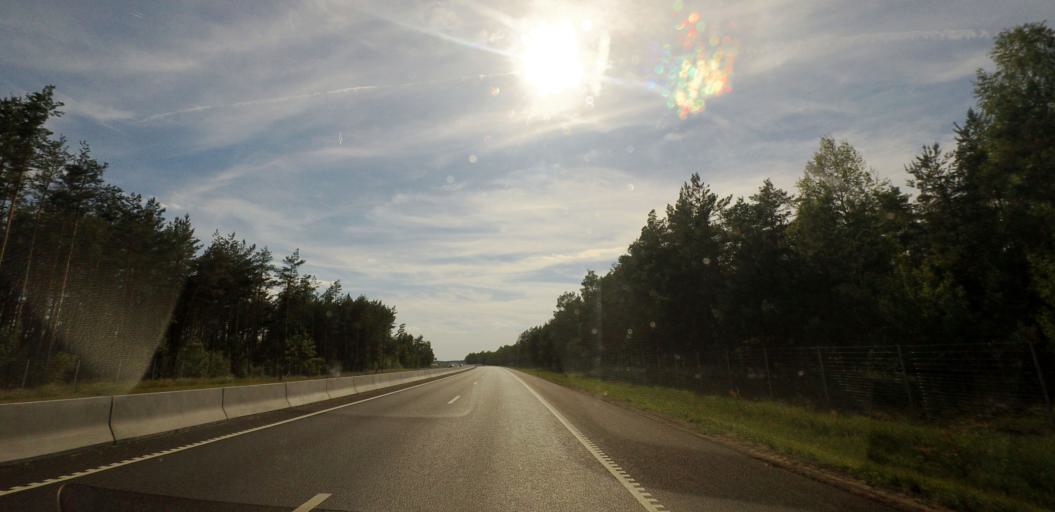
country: BY
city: Berezovka
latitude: 53.8439
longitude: 25.4924
